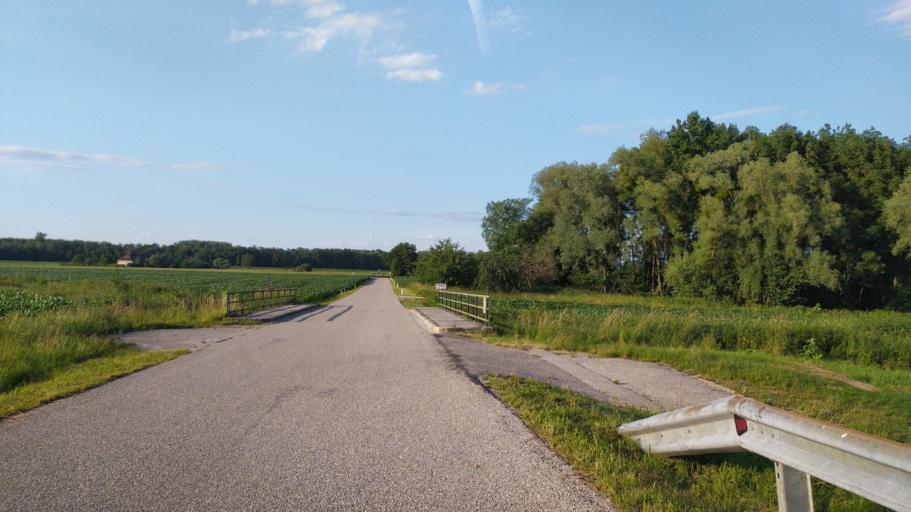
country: AT
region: Lower Austria
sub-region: Politischer Bezirk Amstetten
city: Strengberg
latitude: 48.1707
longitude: 14.6260
